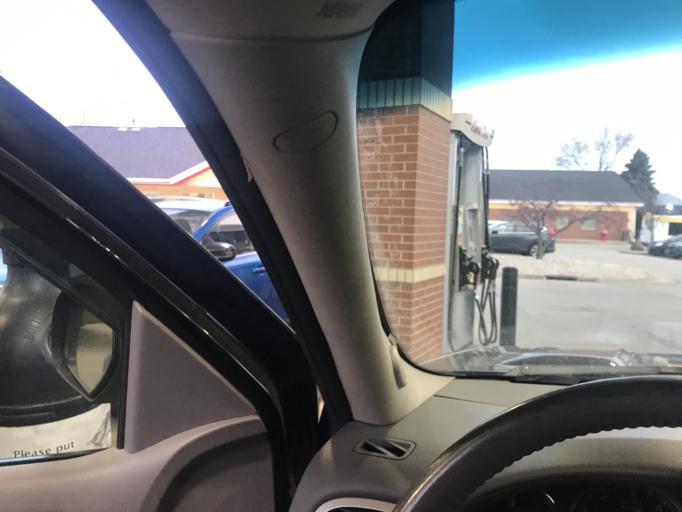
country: US
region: Wisconsin
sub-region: Kenosha County
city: Somers
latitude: 42.5891
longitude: -87.8834
